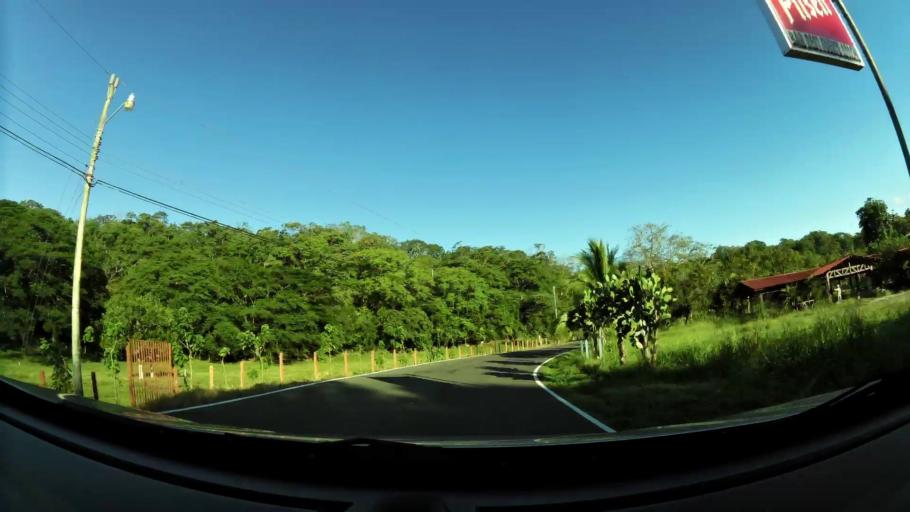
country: CR
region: Puntarenas
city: Miramar
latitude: 10.1286
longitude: -84.8340
